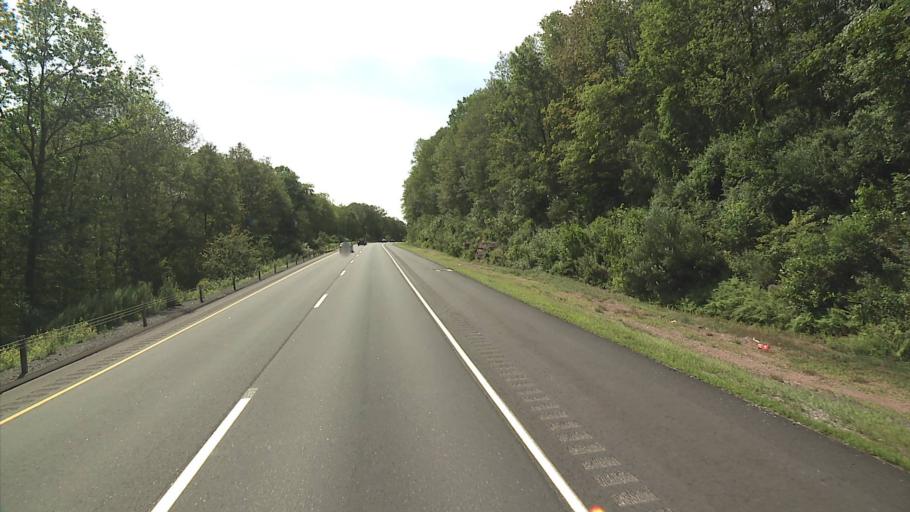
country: US
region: Connecticut
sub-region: Hartford County
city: Terramuggus
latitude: 41.6185
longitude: -72.4374
